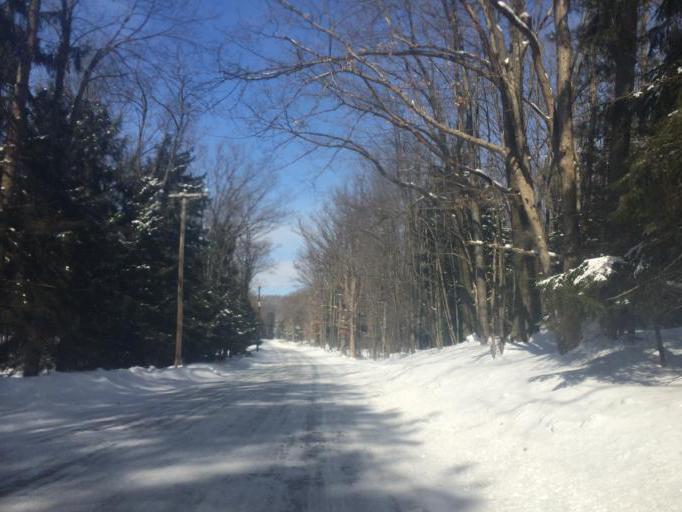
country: US
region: Pennsylvania
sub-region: Centre County
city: Stormstown
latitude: 40.9090
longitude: -78.0550
